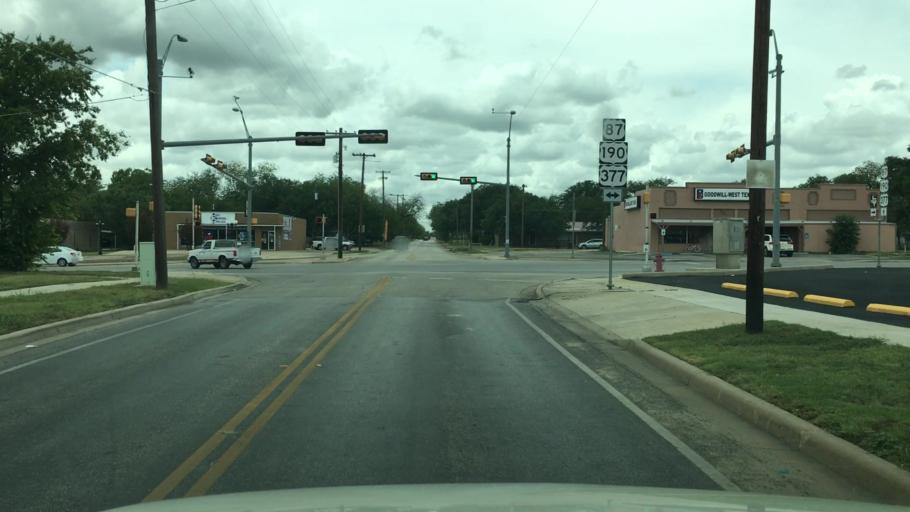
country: US
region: Texas
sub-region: McCulloch County
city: Brady
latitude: 31.1262
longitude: -99.3346
